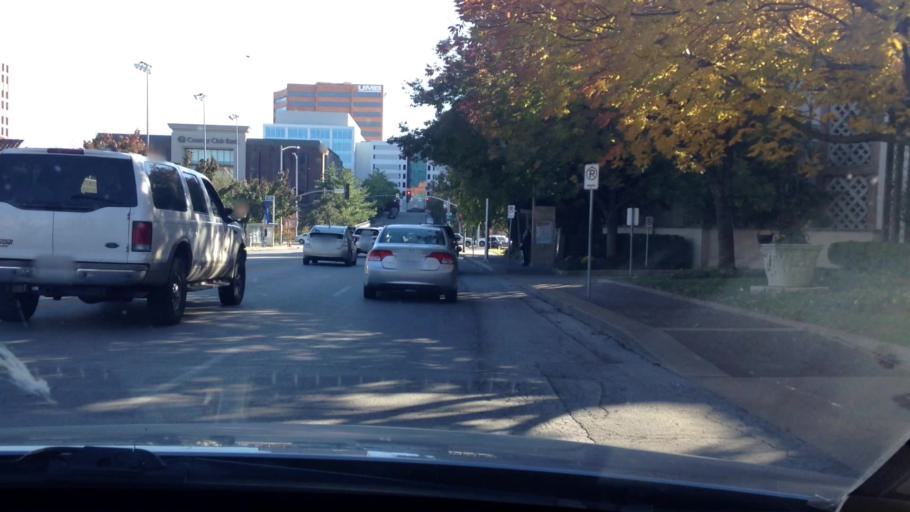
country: US
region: Kansas
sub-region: Johnson County
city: Westwood
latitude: 39.0420
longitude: -94.5881
